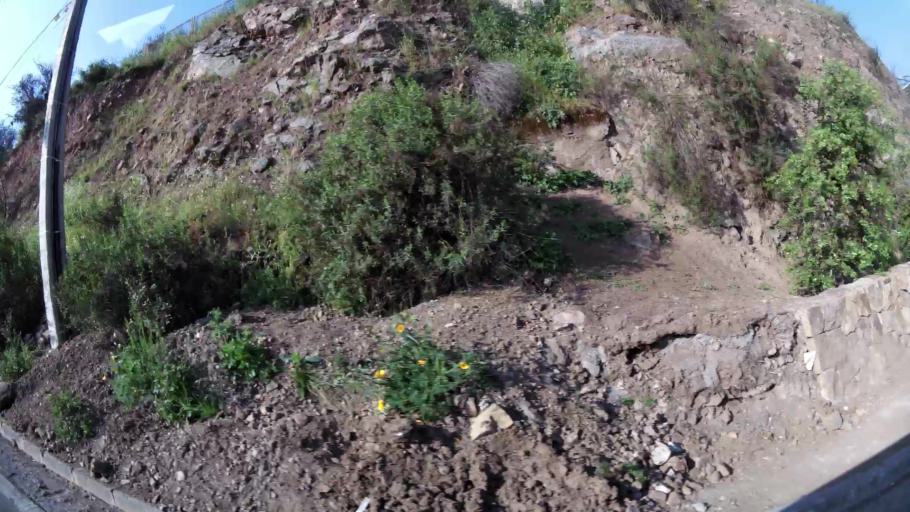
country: CL
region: Santiago Metropolitan
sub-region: Provincia de Santiago
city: Villa Presidente Frei, Nunoa, Santiago, Chile
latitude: -33.3726
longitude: -70.5449
